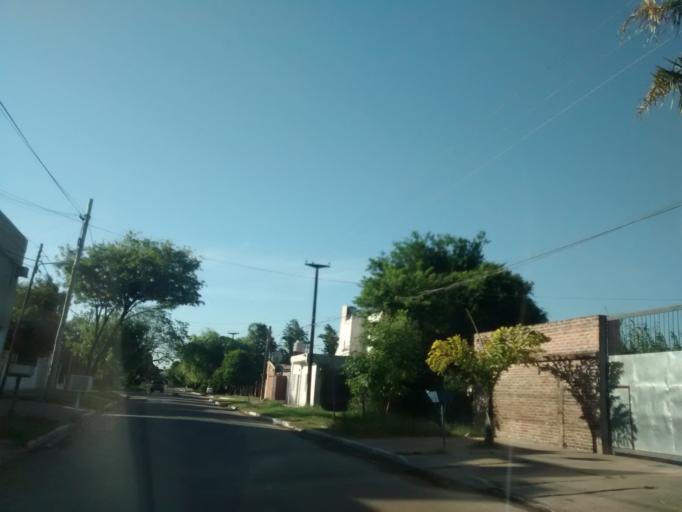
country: AR
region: Chaco
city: Resistencia
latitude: -27.4594
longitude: -59.0015
